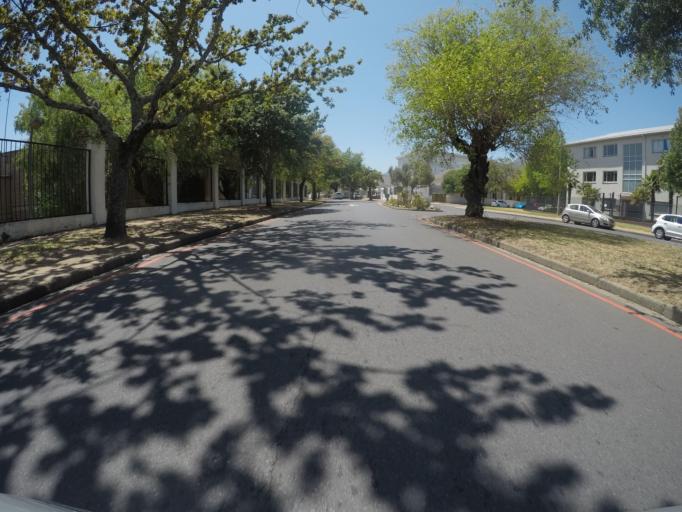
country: ZA
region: Western Cape
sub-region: Cape Winelands District Municipality
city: Stellenbosch
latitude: -33.9362
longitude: 18.8556
